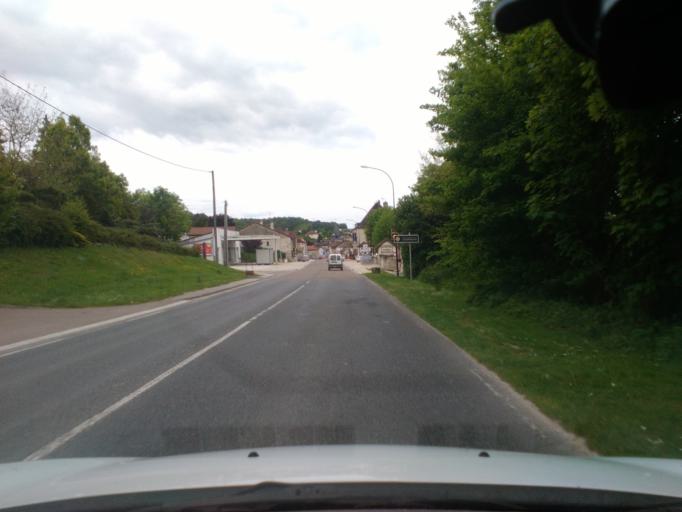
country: FR
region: Champagne-Ardenne
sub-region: Departement de l'Aube
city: Bar-sur-Aube
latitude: 48.2696
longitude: 4.6432
